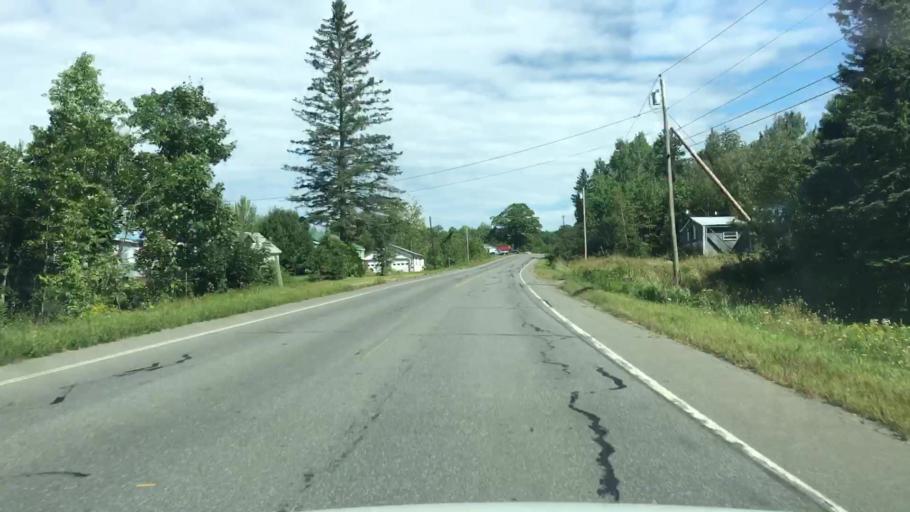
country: US
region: Maine
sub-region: Penobscot County
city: Garland
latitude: 45.0804
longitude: -69.2298
